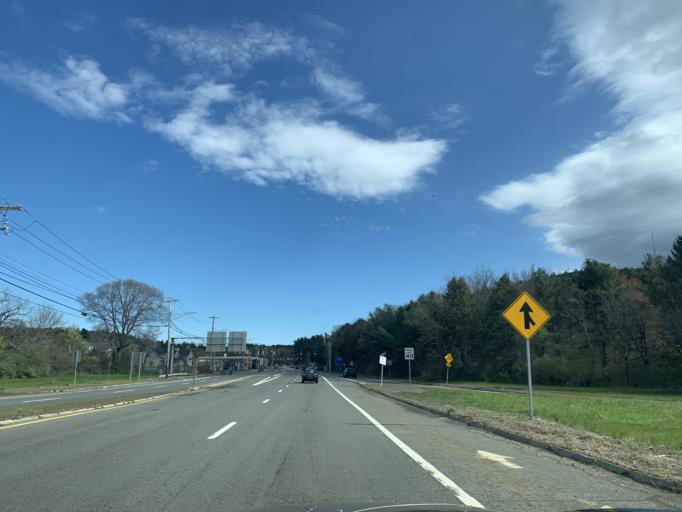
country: US
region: Massachusetts
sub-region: Norfolk County
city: Canton
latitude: 42.2050
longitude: -71.1193
